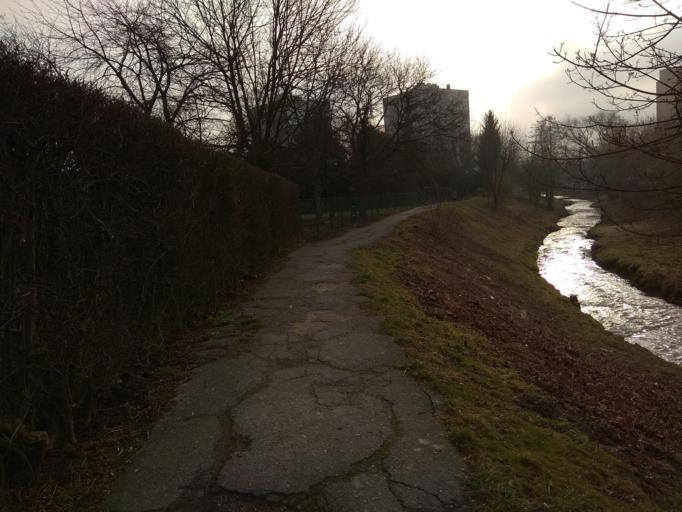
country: PL
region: Lesser Poland Voivodeship
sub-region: Krakow
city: Krakow
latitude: 50.0749
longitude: 19.9637
